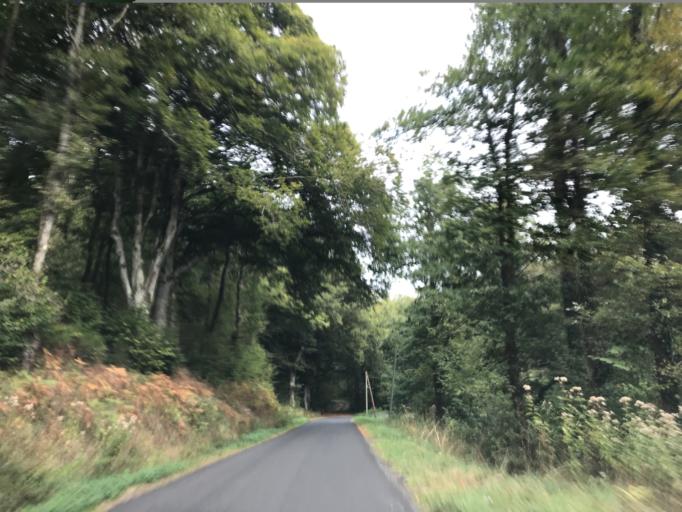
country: FR
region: Auvergne
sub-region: Departement du Puy-de-Dome
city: Celles-sur-Durolle
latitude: 45.8252
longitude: 3.6240
